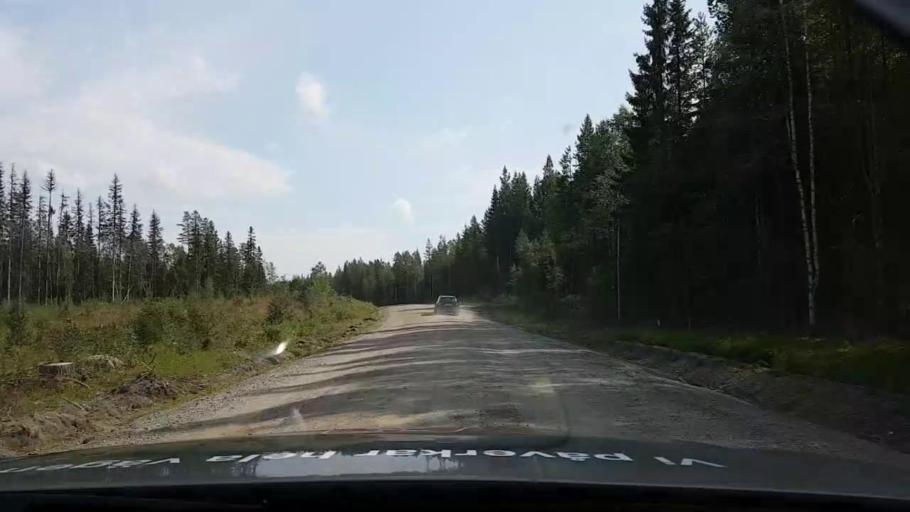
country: SE
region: Jaemtland
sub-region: Braecke Kommun
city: Braecke
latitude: 62.7375
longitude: 15.4564
